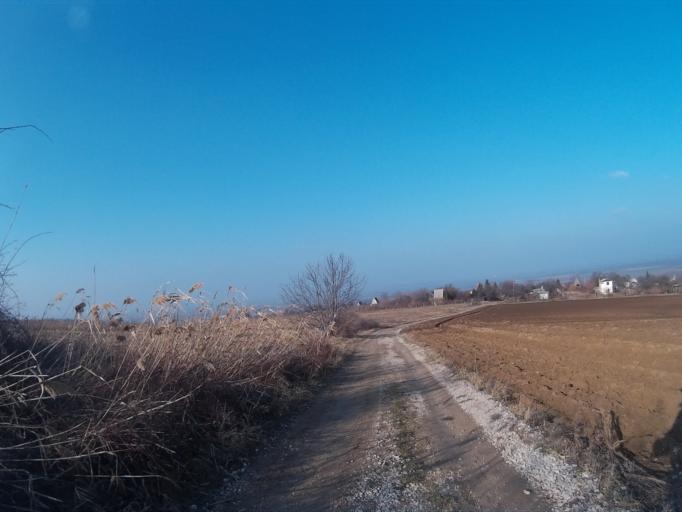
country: HU
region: Komarom-Esztergom
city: Labatlan
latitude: 47.7403
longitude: 18.4814
